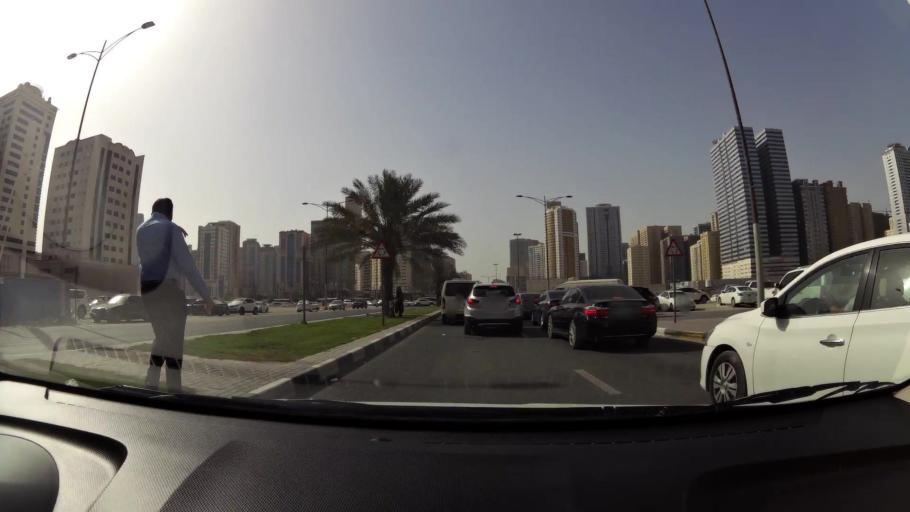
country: AE
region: Ash Shariqah
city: Sharjah
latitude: 25.3073
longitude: 55.3717
